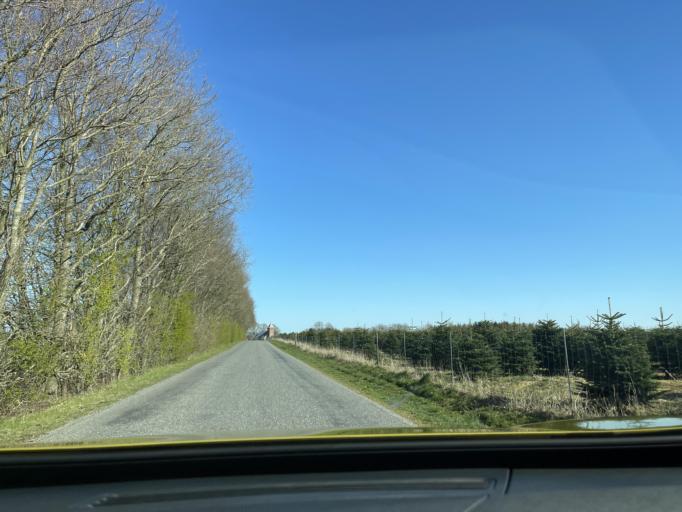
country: DK
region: Central Jutland
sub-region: Silkeborg Kommune
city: Kjellerup
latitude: 56.2462
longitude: 9.4815
